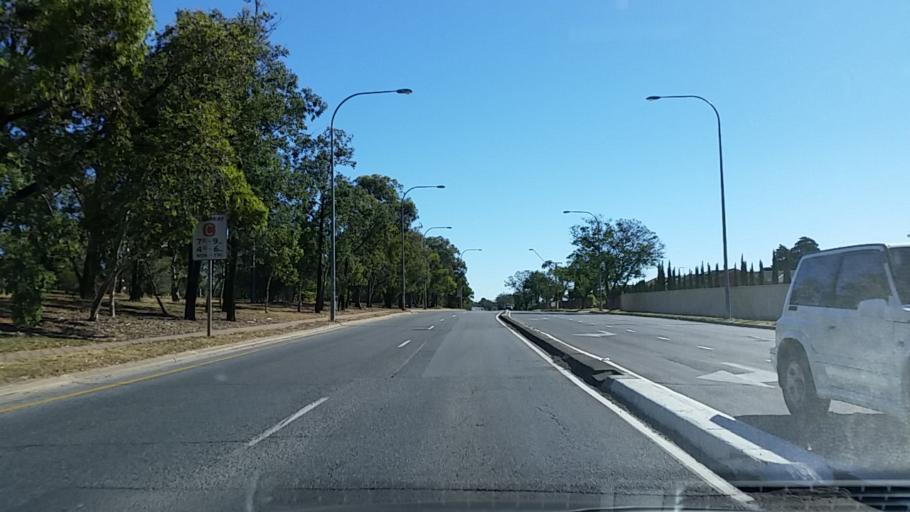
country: AU
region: South Australia
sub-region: Salisbury
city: Ingle Farm
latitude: -34.8245
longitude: 138.6355
